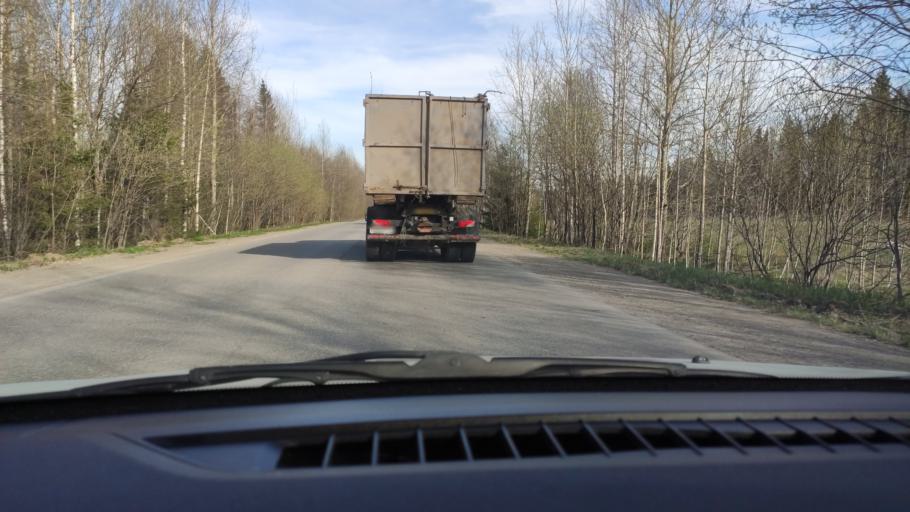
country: RU
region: Perm
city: Ferma
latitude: 57.9385
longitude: 56.4551
